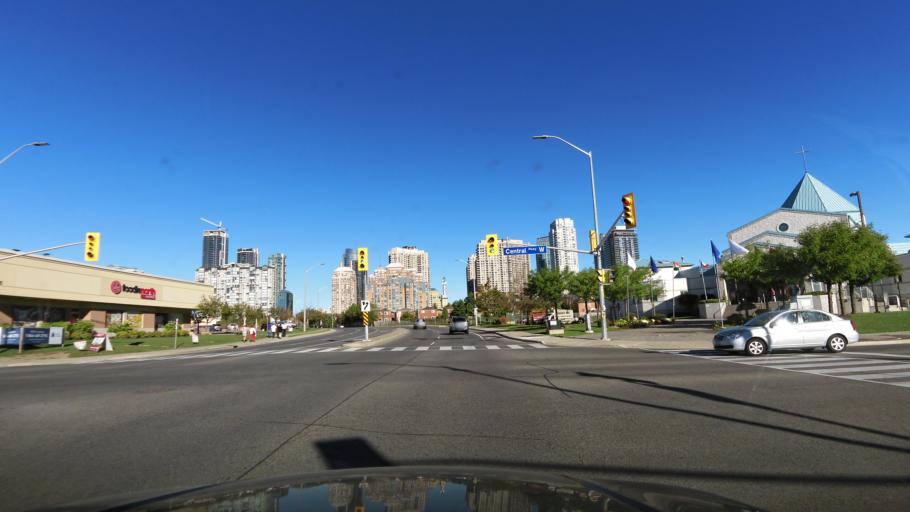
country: CA
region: Ontario
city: Mississauga
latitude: 43.5833
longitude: -79.6360
